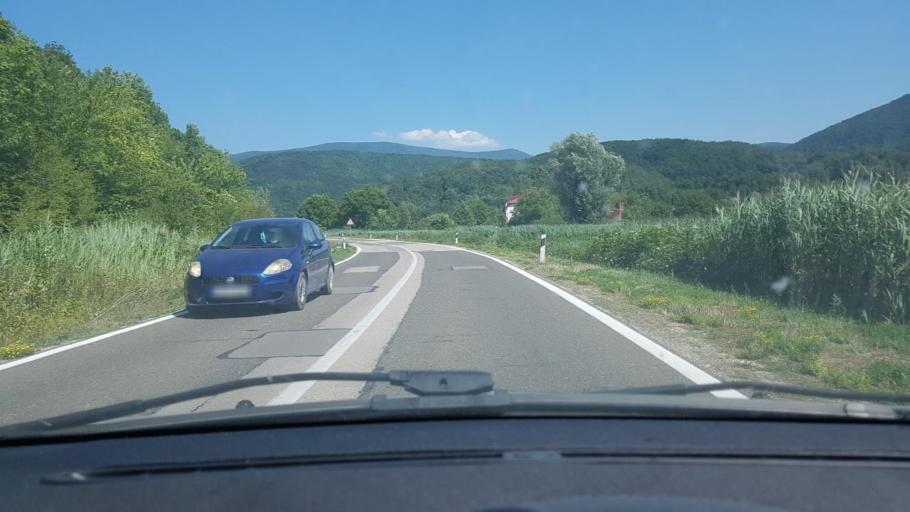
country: BA
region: Federation of Bosnia and Herzegovina
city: Bihac
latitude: 44.7510
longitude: 15.9369
